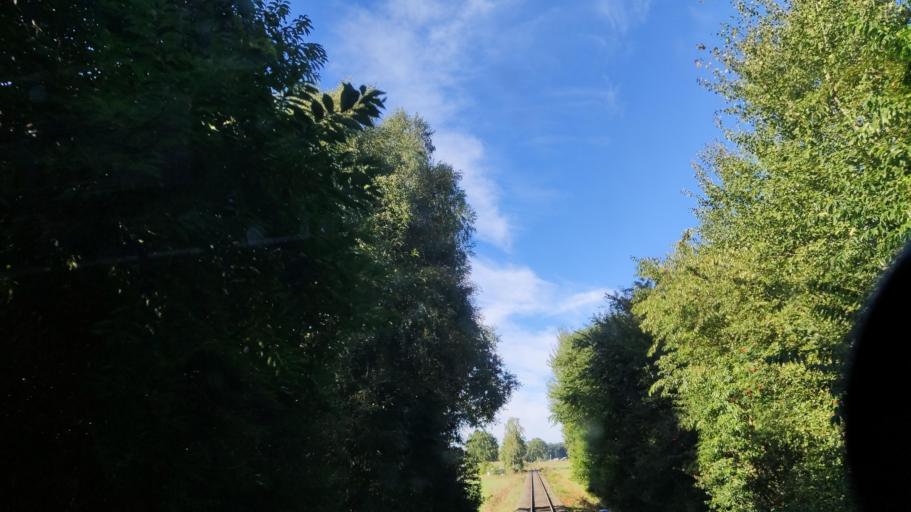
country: DE
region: Lower Saxony
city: Soderstorf
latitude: 53.1302
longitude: 10.1331
